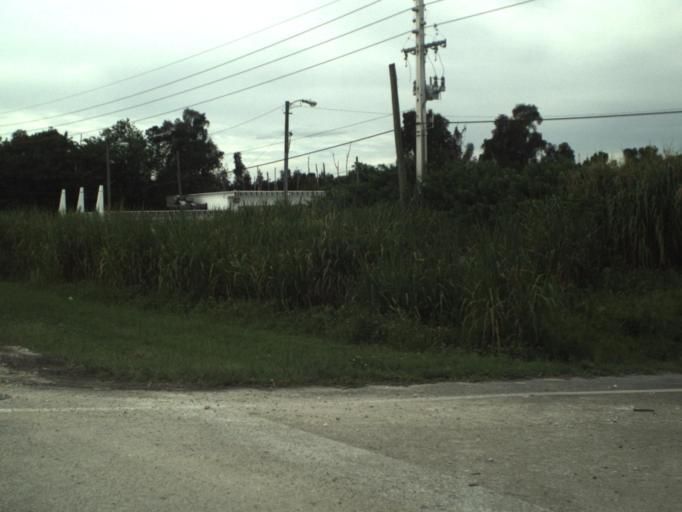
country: US
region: Florida
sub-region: Miami-Dade County
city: Kendall West
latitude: 25.7603
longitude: -80.4814
